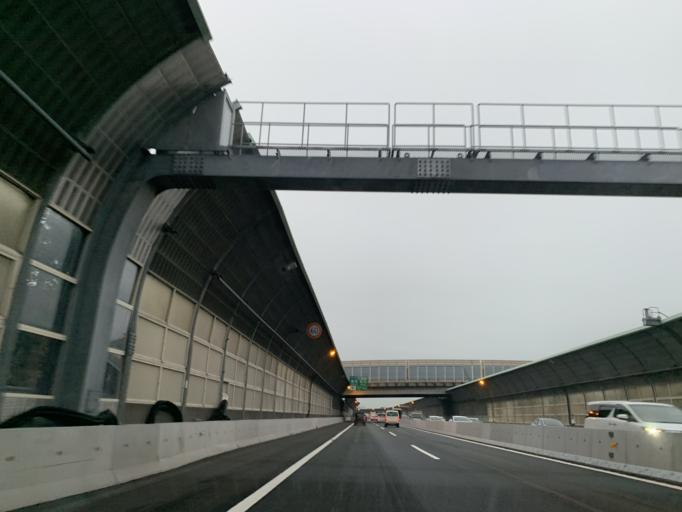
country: JP
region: Chiba
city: Funabashi
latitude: 35.6724
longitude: 140.0200
